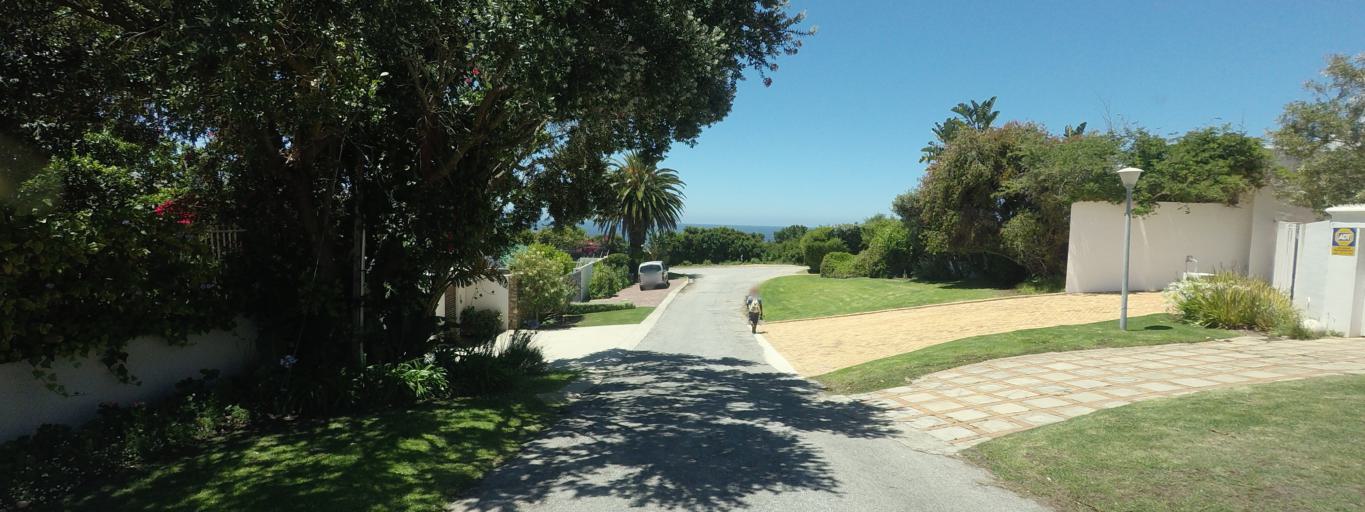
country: ZA
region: Western Cape
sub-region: Eden District Municipality
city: Plettenberg Bay
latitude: -34.0533
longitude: 23.3770
